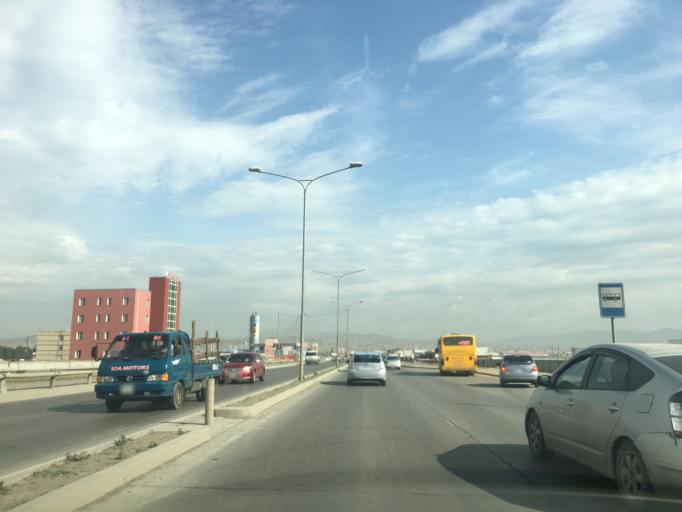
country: MN
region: Ulaanbaatar
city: Ulaanbaatar
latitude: 47.8923
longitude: 106.7854
